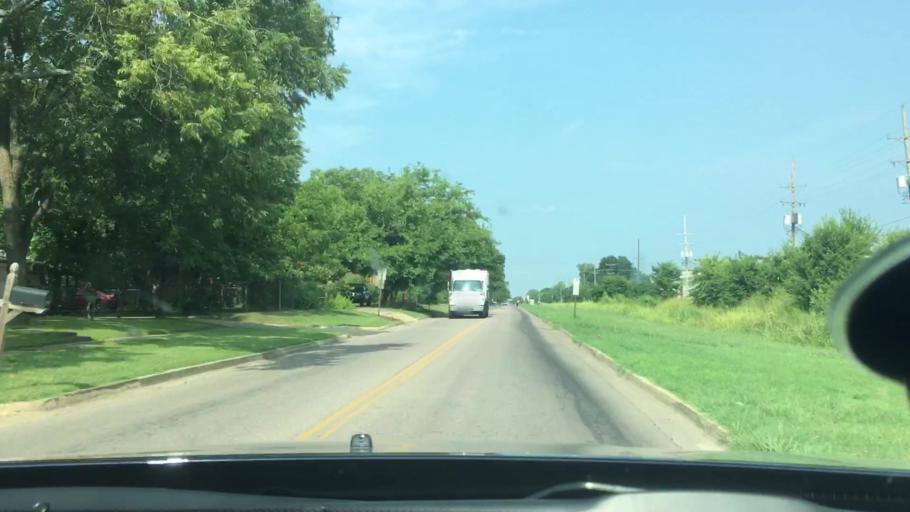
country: US
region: Oklahoma
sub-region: Bryan County
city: Durant
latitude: 33.9917
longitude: -96.3863
